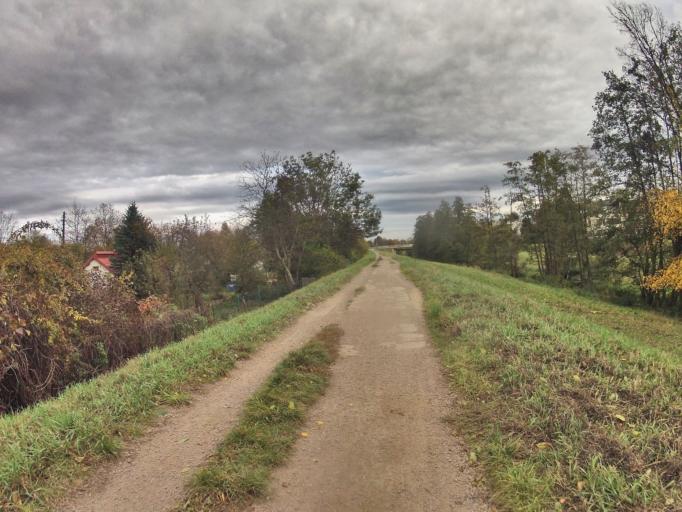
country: PL
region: Lesser Poland Voivodeship
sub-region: Krakow
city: Krakow
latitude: 50.0615
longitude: 19.8977
